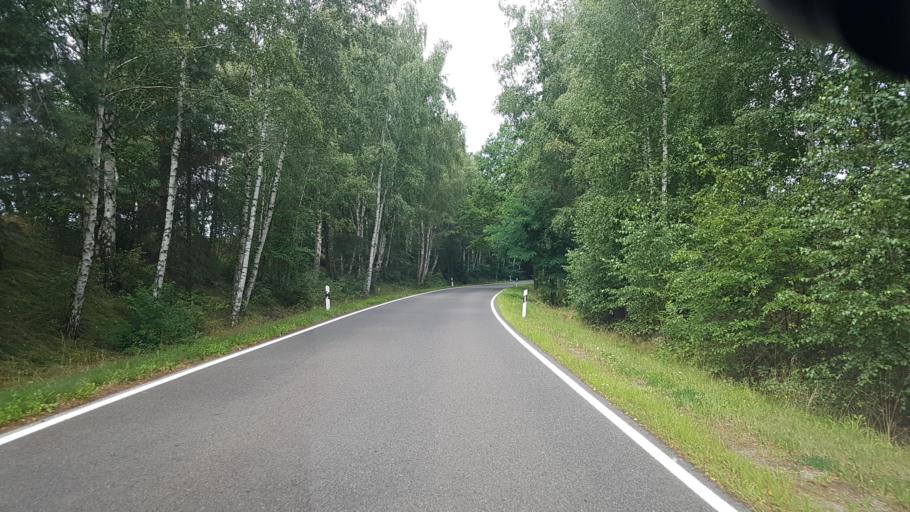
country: DE
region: Brandenburg
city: Spremberg
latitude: 51.5888
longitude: 14.3505
